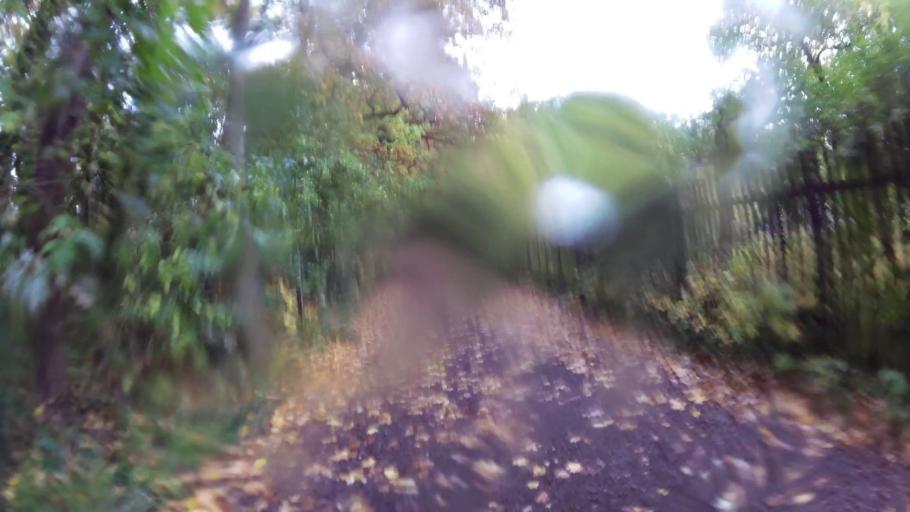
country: DE
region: Thuringia
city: Weimar
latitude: 50.9735
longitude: 11.3171
